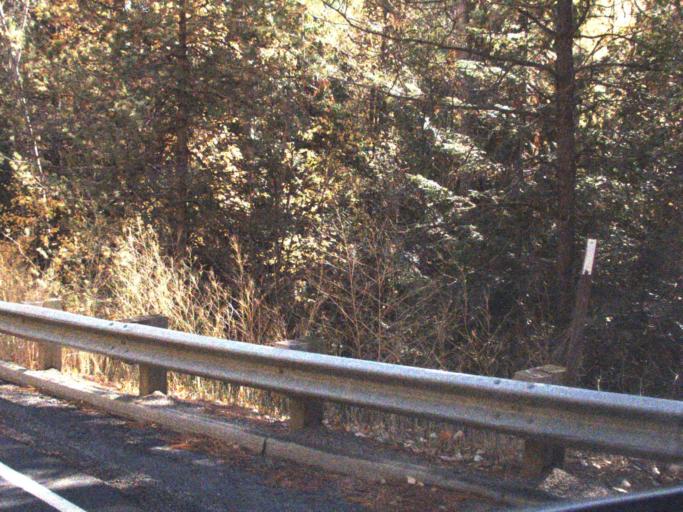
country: US
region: Washington
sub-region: Stevens County
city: Kettle Falls
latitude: 48.6031
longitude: -118.3576
